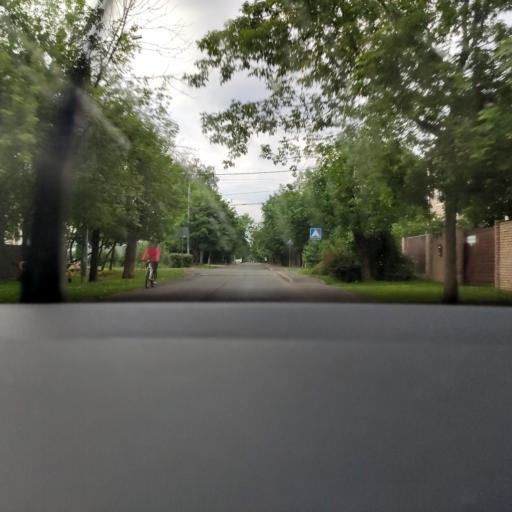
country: RU
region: Moscow
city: Vagonoremont
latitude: 55.9035
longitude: 37.5588
